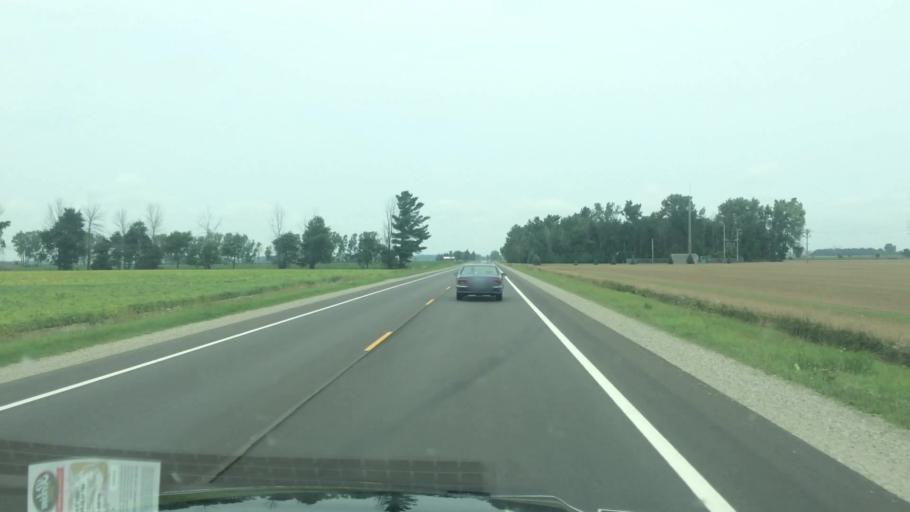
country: US
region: Michigan
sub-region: Huron County
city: Bad Axe
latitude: 43.9840
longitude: -83.0070
